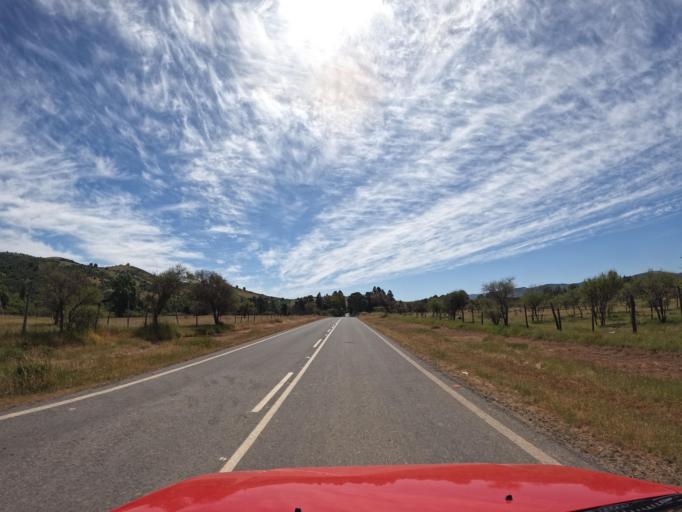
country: CL
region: Maule
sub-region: Provincia de Talca
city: Talca
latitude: -35.0264
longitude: -71.7672
